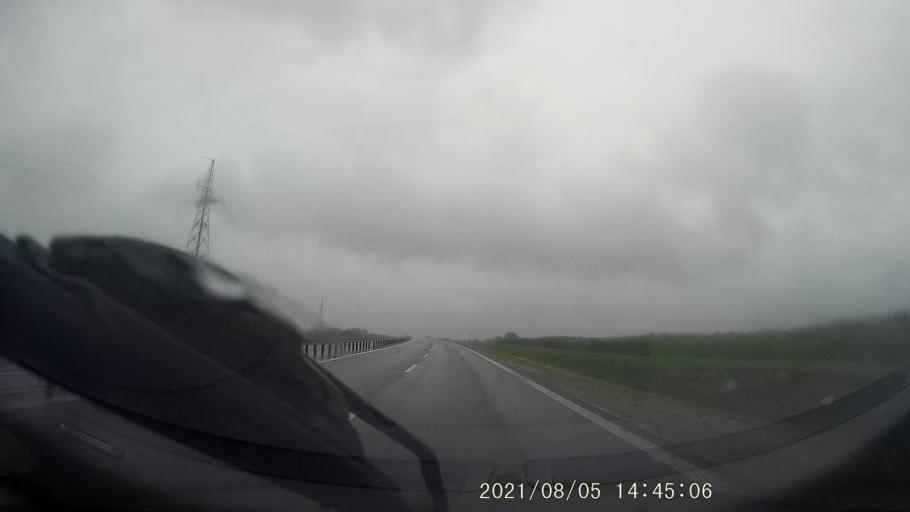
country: PL
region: Opole Voivodeship
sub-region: Powiat nyski
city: Nysa
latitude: 50.4979
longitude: 17.3668
